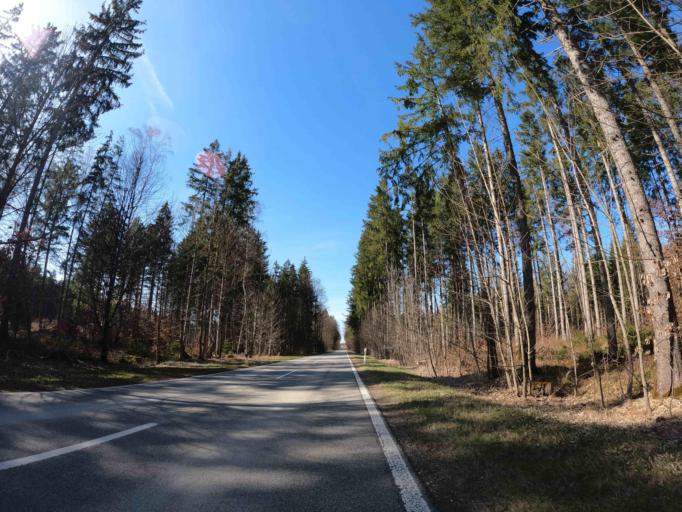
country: DE
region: Bavaria
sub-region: Upper Bavaria
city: Oberhaching
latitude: 48.0101
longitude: 11.6168
